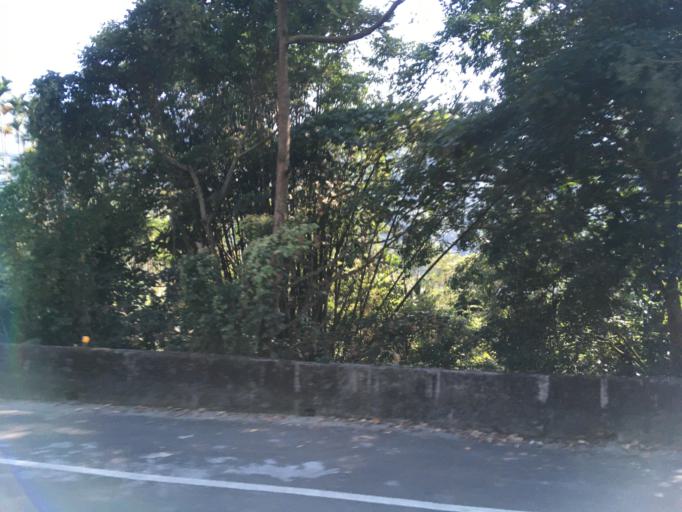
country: TW
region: Taiwan
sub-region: Chiayi
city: Jiayi Shi
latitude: 23.4343
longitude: 120.6320
